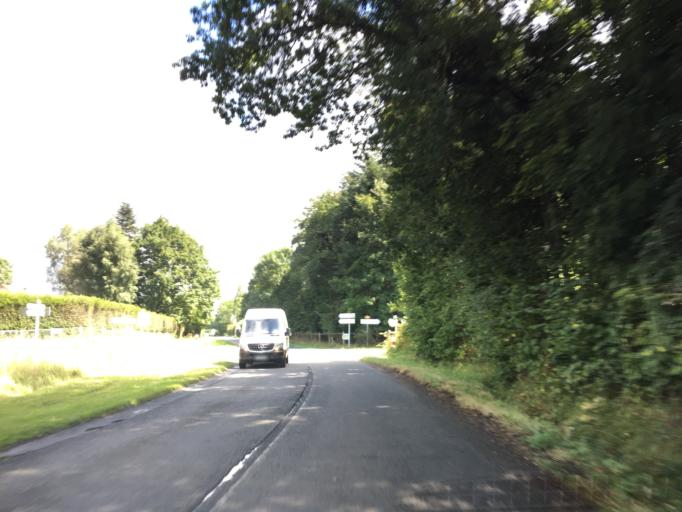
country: FR
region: Lower Normandy
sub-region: Departement du Calvados
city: Dozule
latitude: 49.2700
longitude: -0.0420
